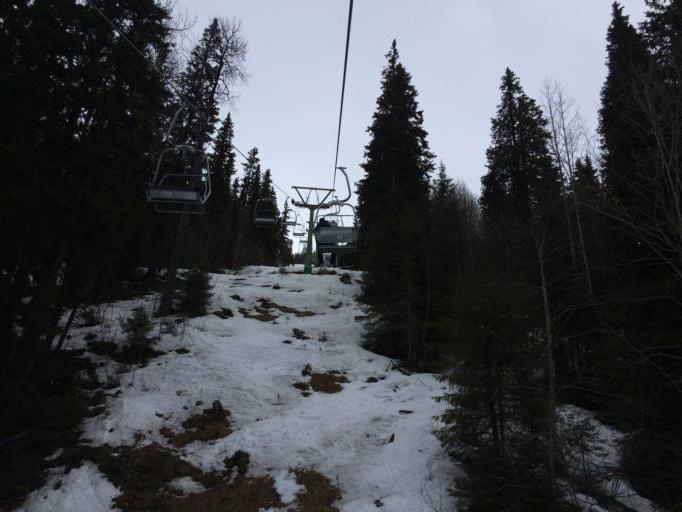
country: SE
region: Jaemtland
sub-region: Are Kommun
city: Are
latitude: 63.4055
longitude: 13.0779
